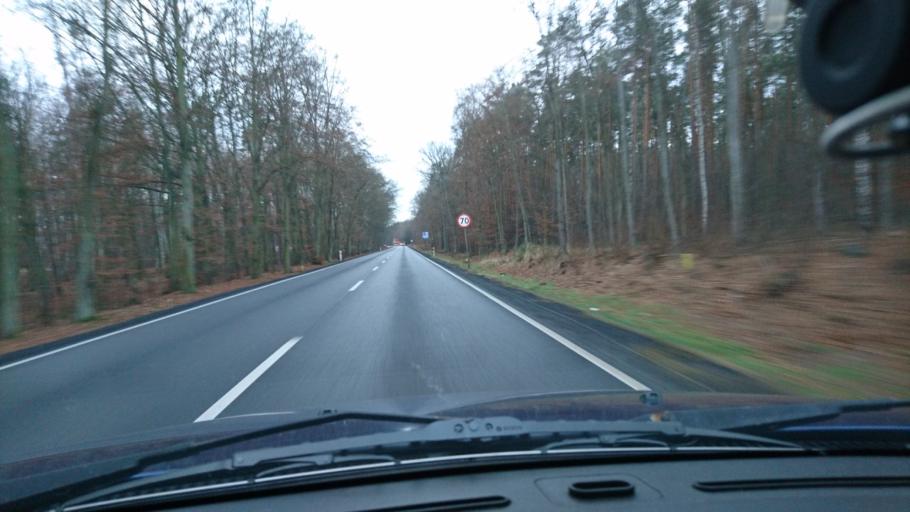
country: PL
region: Opole Voivodeship
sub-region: Powiat kluczborski
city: Kluczbork
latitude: 50.9630
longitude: 18.2846
